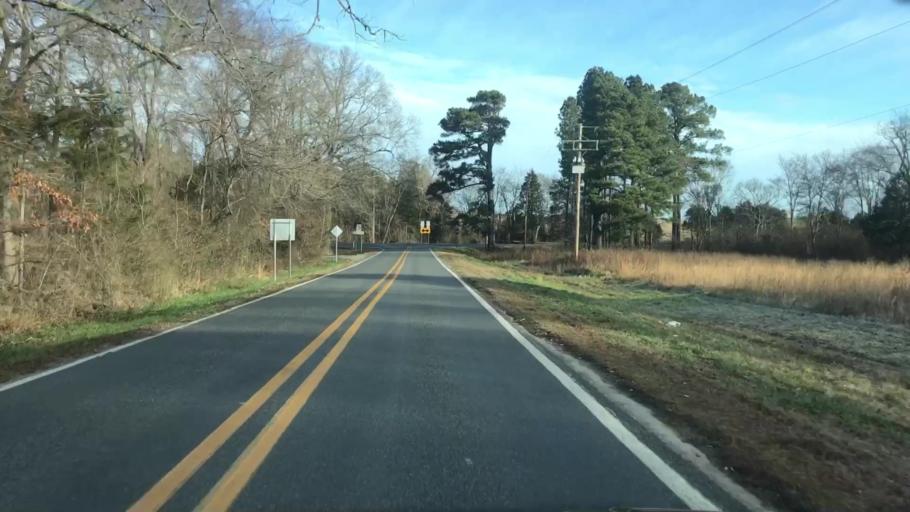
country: US
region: Arkansas
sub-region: Garland County
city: Rockwell
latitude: 34.5096
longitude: -93.2760
